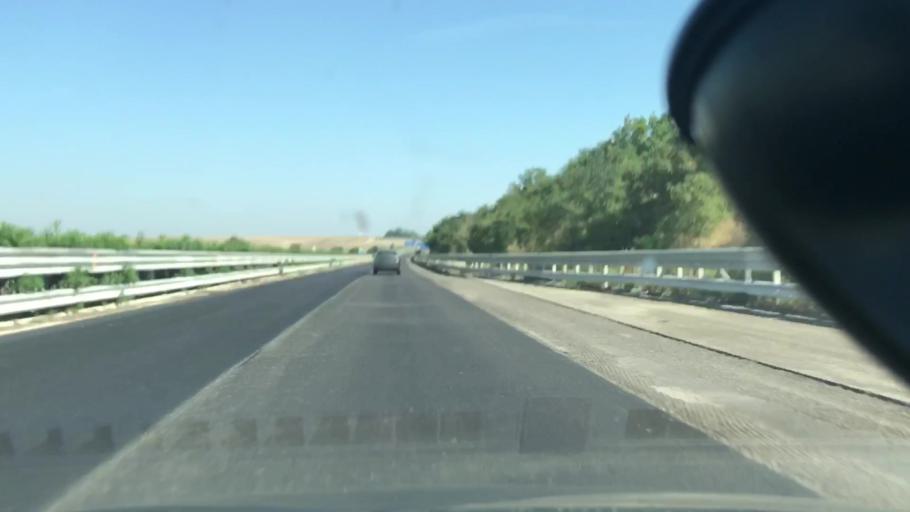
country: IT
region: Apulia
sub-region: Provincia di Foggia
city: Ordona
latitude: 41.2975
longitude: 15.5544
